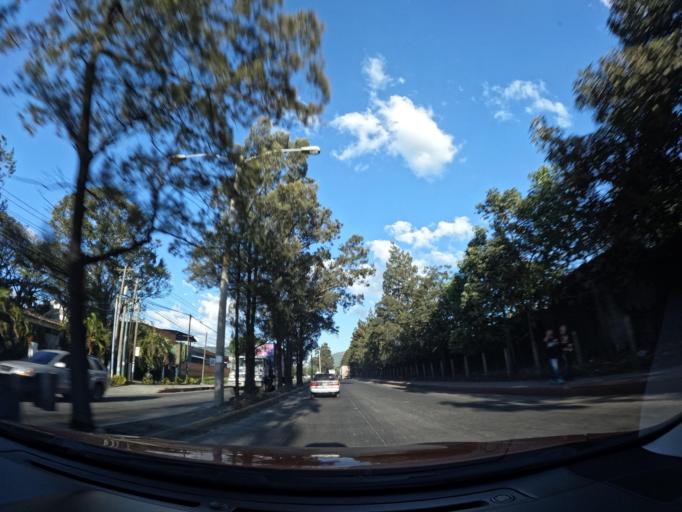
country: GT
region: Escuintla
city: Palin
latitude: 14.4069
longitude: -90.6889
